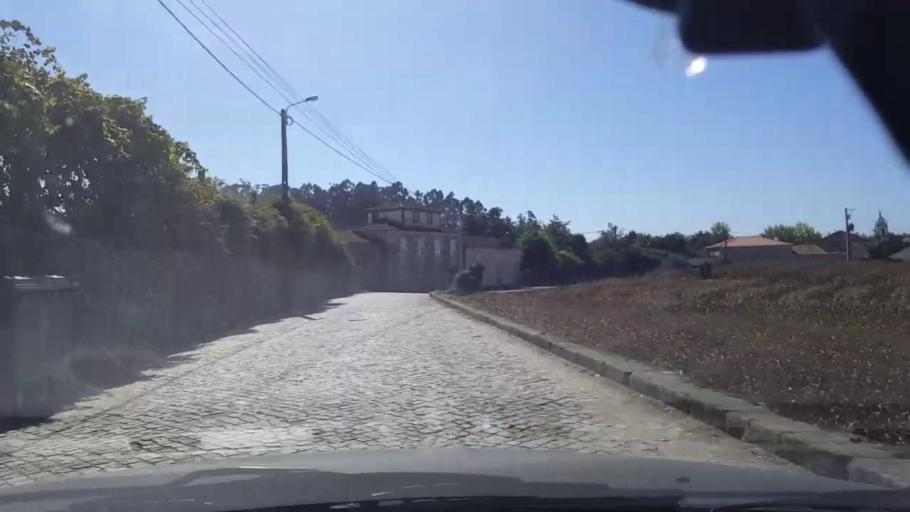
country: PT
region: Porto
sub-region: Maia
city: Gemunde
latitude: 41.2967
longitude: -8.6843
